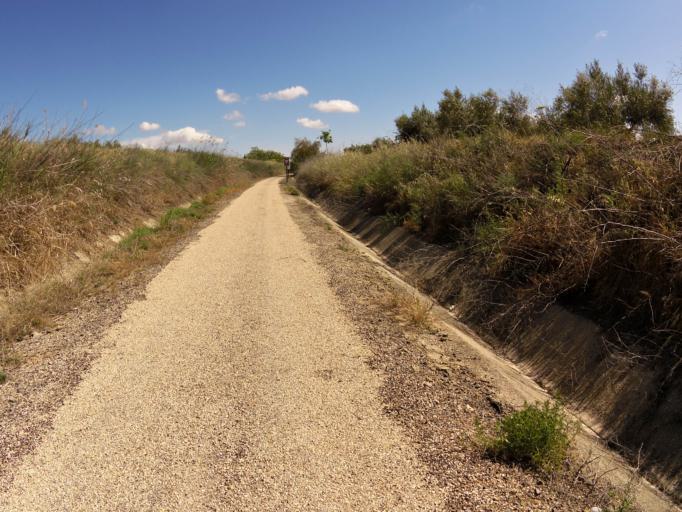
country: ES
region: Andalusia
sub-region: Provincia de Jaen
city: Alcaudete
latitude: 37.6061
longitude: -4.1292
